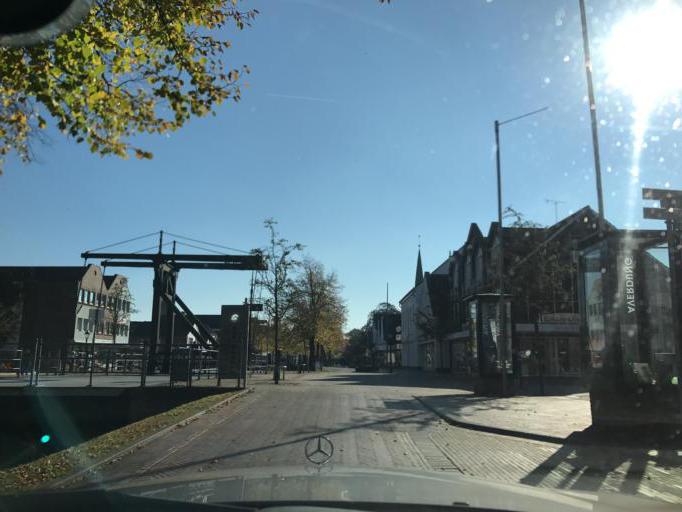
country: DE
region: Lower Saxony
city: Papenburg
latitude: 53.0825
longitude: 7.3908
